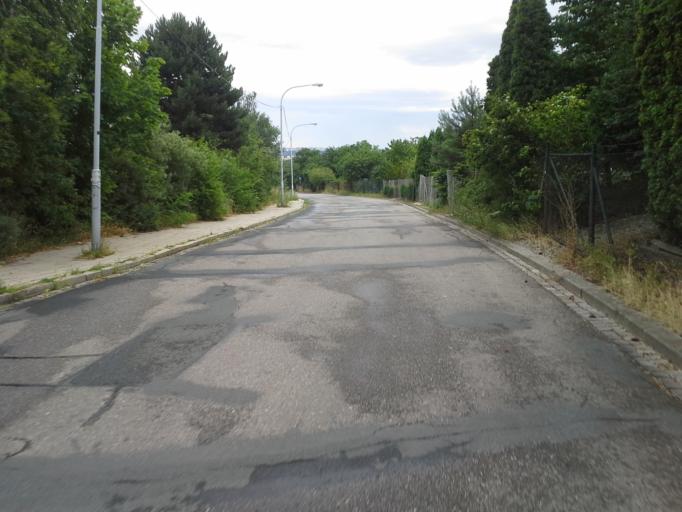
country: CZ
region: South Moravian
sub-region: Mesto Brno
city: Mokra Hora
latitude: 49.2234
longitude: 16.5756
